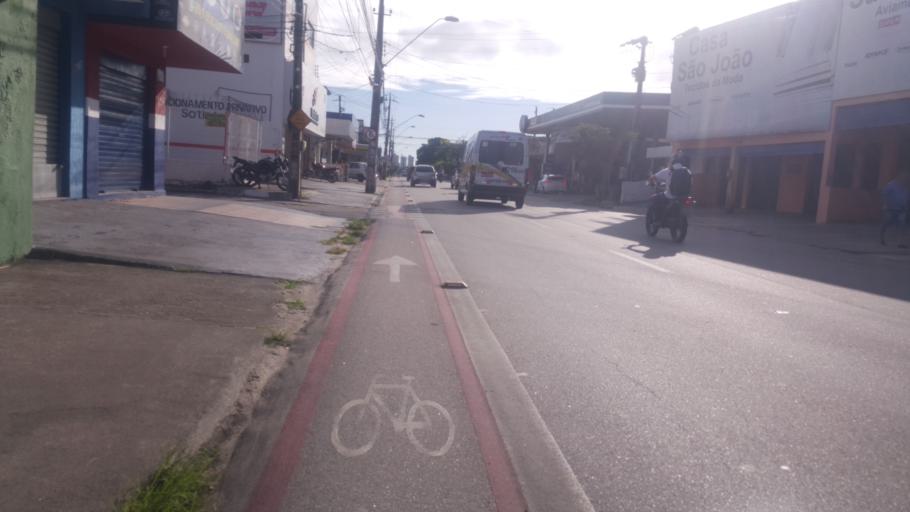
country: BR
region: Ceara
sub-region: Fortaleza
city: Fortaleza
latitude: -3.7614
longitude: -38.5455
